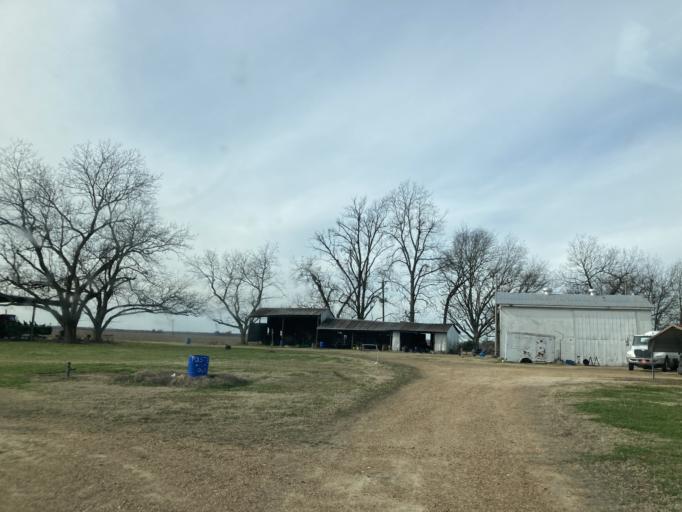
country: US
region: Mississippi
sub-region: Humphreys County
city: Belzoni
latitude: 33.1304
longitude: -90.6113
